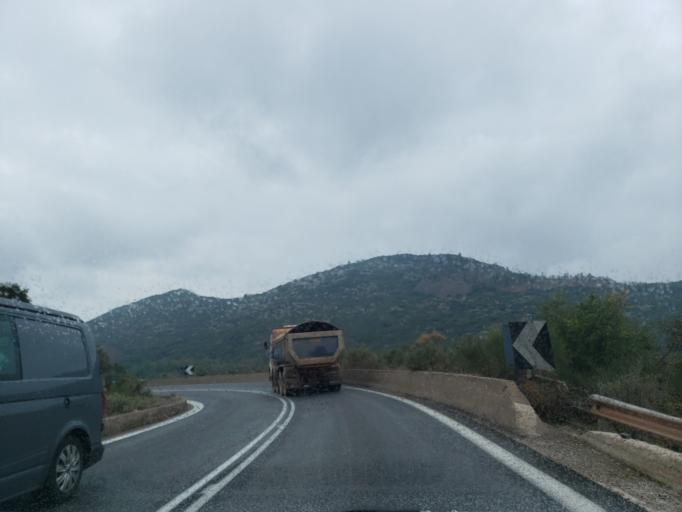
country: GR
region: Central Greece
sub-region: Nomos Fokidos
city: Amfissa
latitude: 38.5752
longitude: 22.3940
